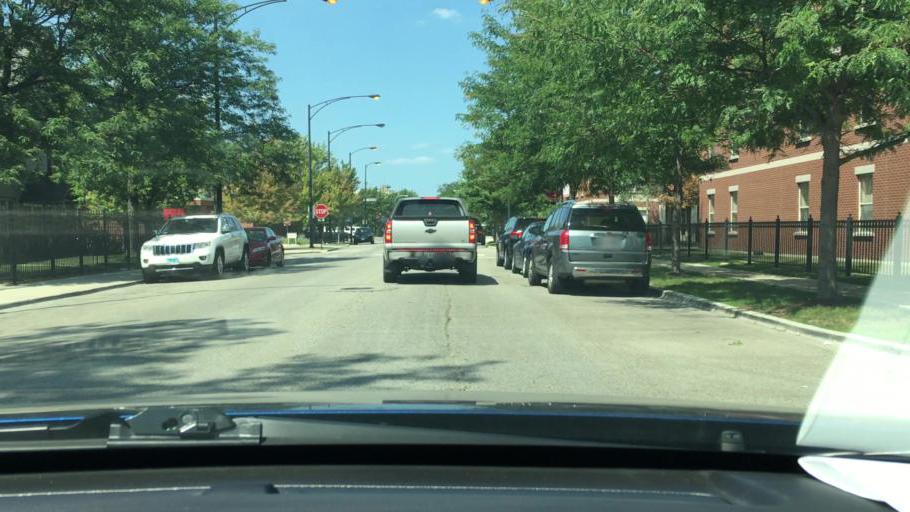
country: US
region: Illinois
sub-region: Cook County
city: Chicago
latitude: 41.8657
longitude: -87.6566
